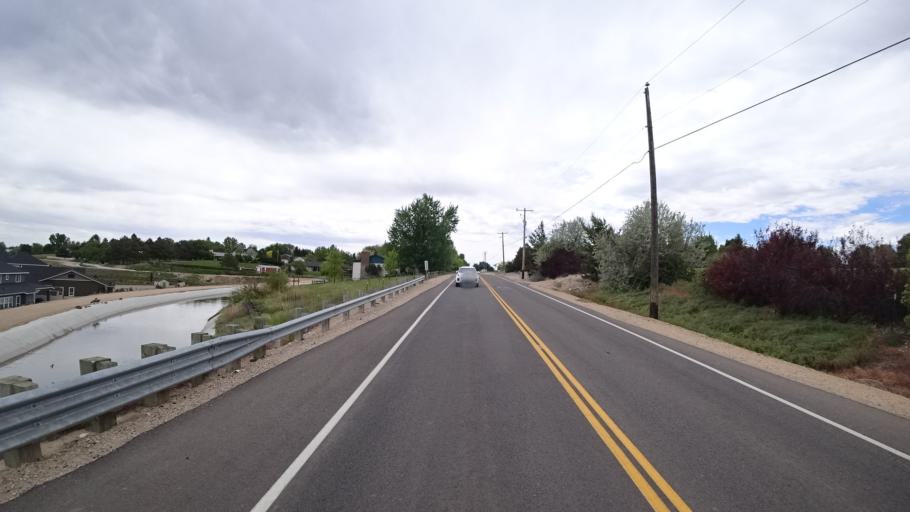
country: US
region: Idaho
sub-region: Ada County
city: Meridian
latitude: 43.5817
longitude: -116.4137
